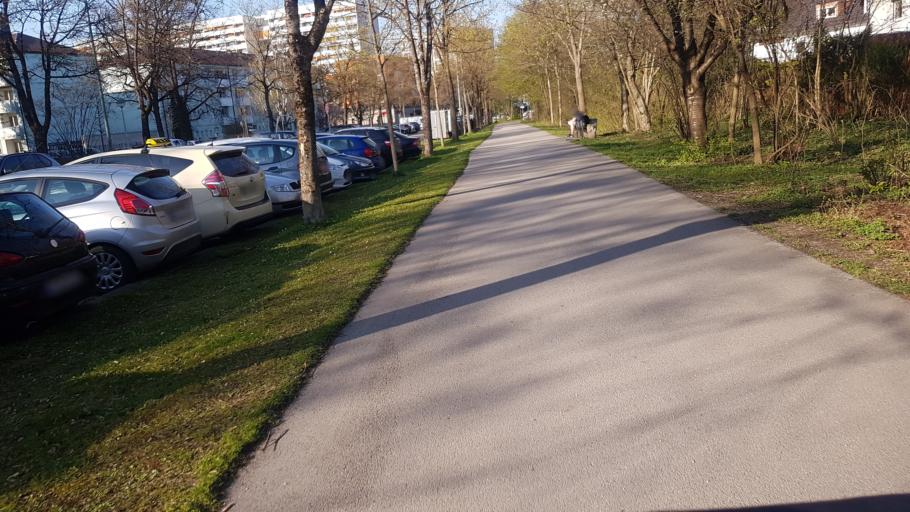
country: DE
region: Bavaria
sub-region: Upper Bavaria
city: Neuried
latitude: 48.0935
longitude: 11.4941
